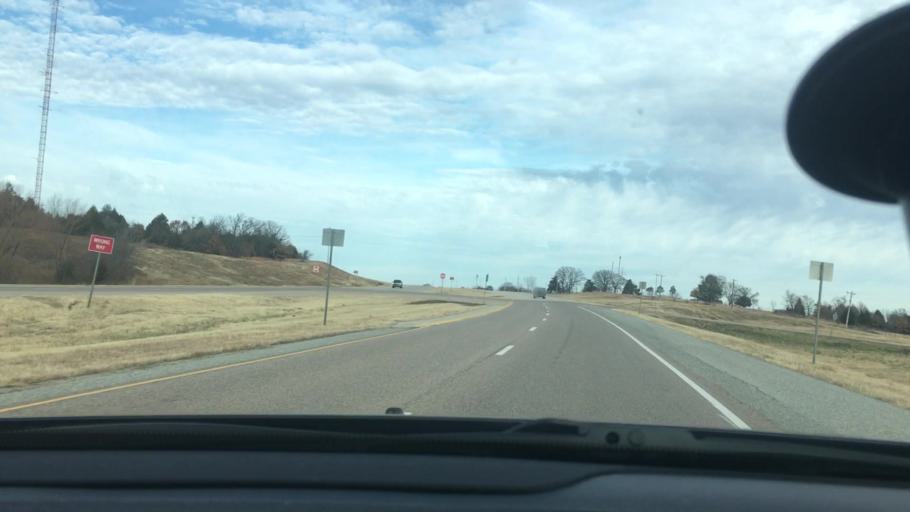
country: US
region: Oklahoma
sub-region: Pontotoc County
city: Byng
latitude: 34.8986
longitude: -96.6747
